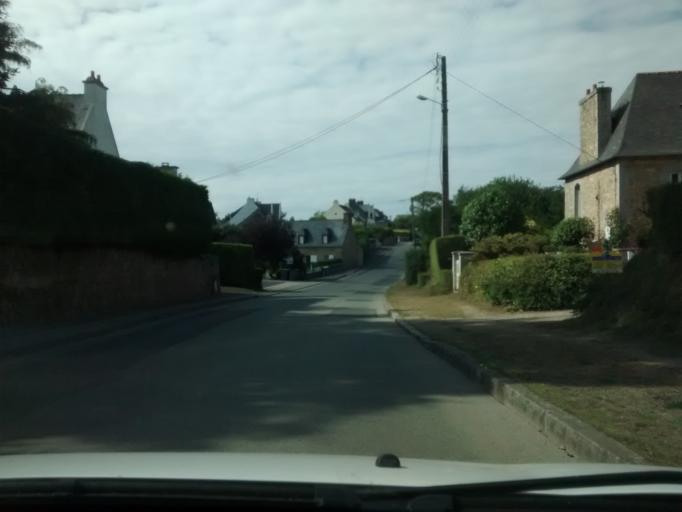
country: FR
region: Brittany
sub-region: Departement des Cotes-d'Armor
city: Penvenan
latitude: 48.8057
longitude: -3.2932
